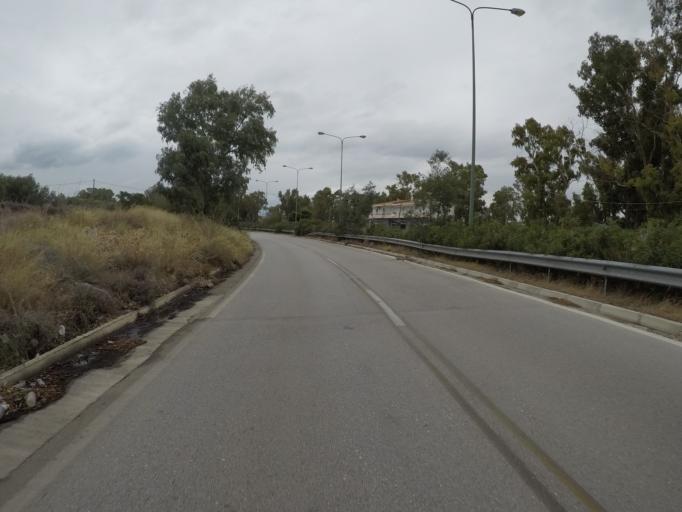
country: GR
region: Peloponnese
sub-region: Nomos Korinthias
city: Korinthos
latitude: 37.9405
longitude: 22.9793
